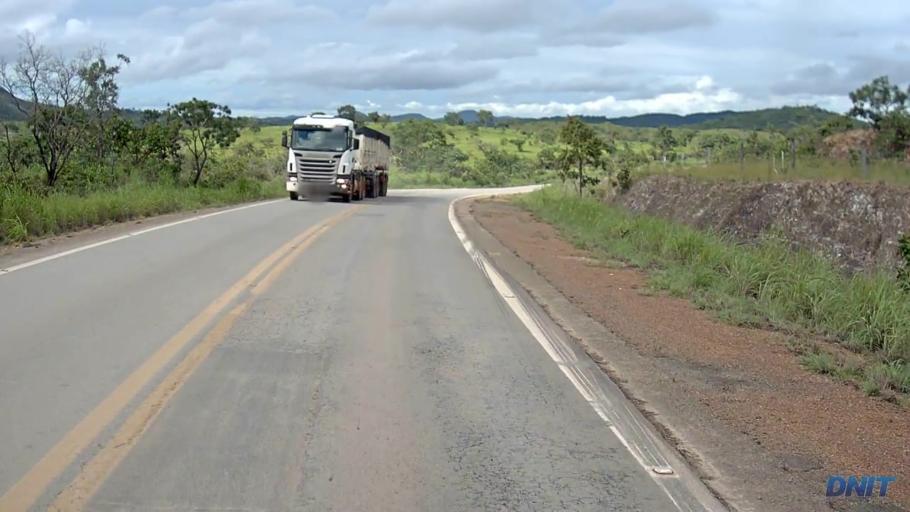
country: BR
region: Goias
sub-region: Padre Bernardo
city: Padre Bernardo
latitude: -15.4666
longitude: -48.2272
